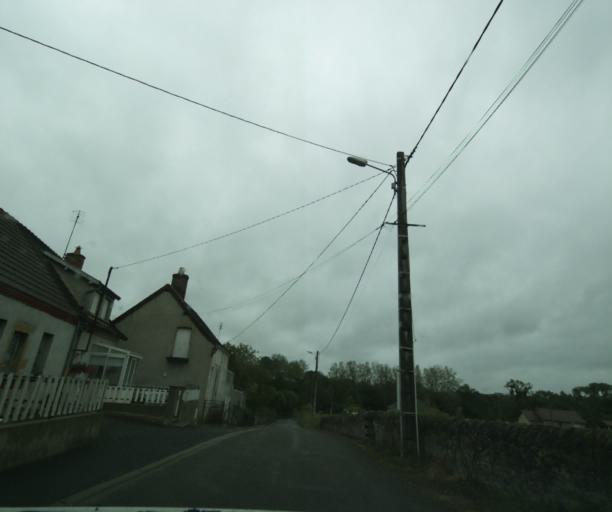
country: FR
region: Bourgogne
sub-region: Departement de Saone-et-Loire
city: Palinges
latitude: 46.5634
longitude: 4.2243
